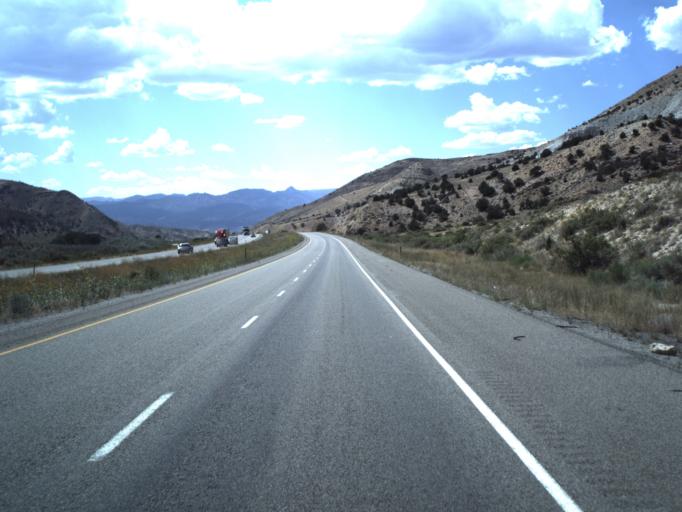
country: US
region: Utah
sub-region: Sevier County
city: Salina
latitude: 38.9331
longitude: -111.7976
